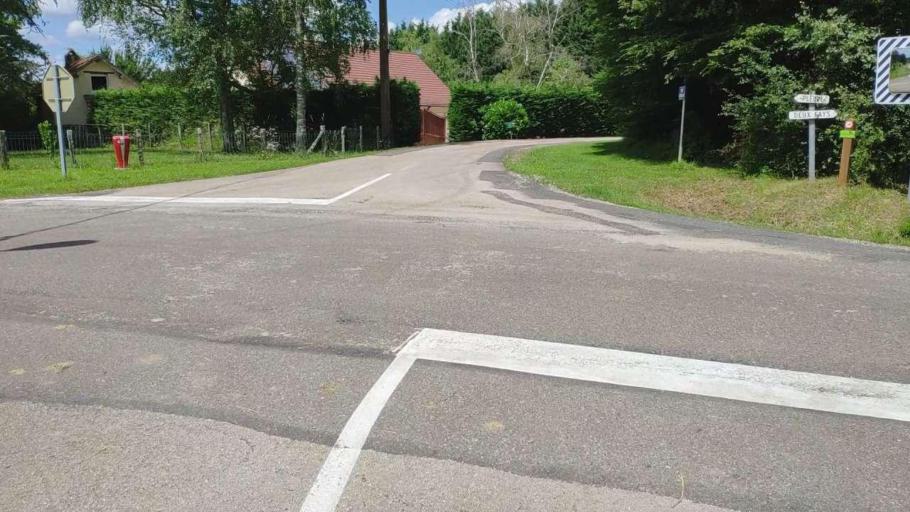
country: FR
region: Franche-Comte
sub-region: Departement du Jura
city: Chaussin
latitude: 46.8854
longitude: 5.4646
